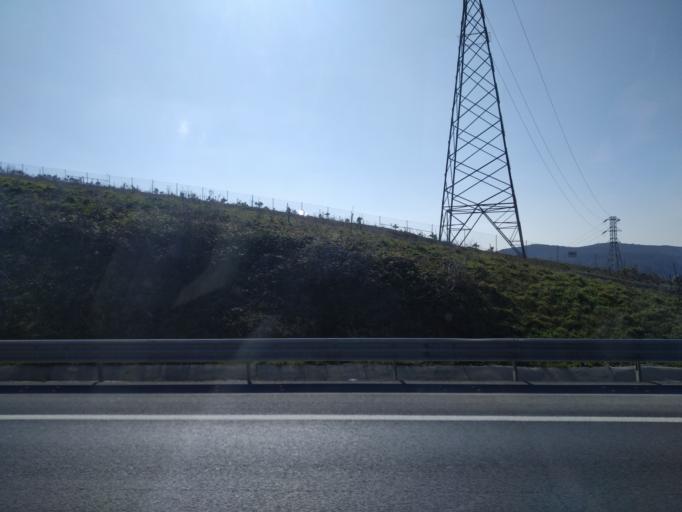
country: TR
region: Istanbul
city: Mahmut Sevket Pasa
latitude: 41.1863
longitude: 29.2163
